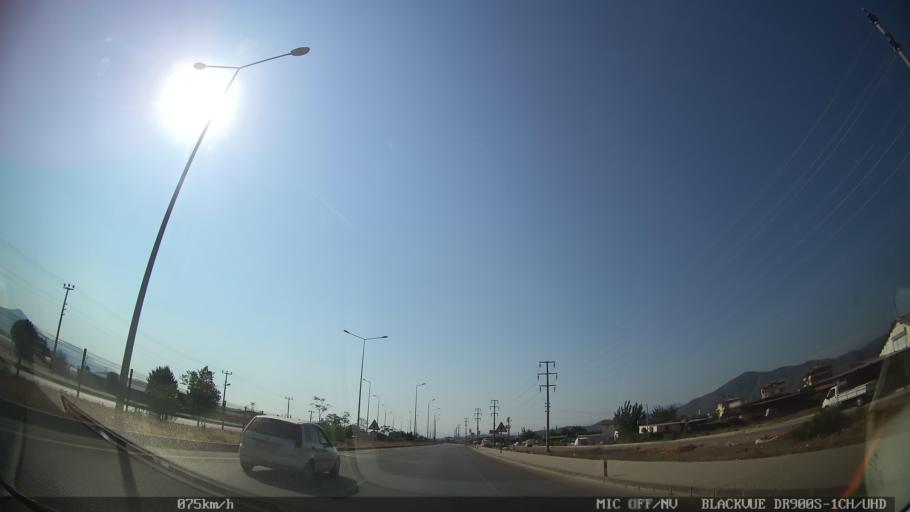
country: TR
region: Mugla
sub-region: Fethiye
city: Fethiye
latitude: 36.6547
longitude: 29.1666
